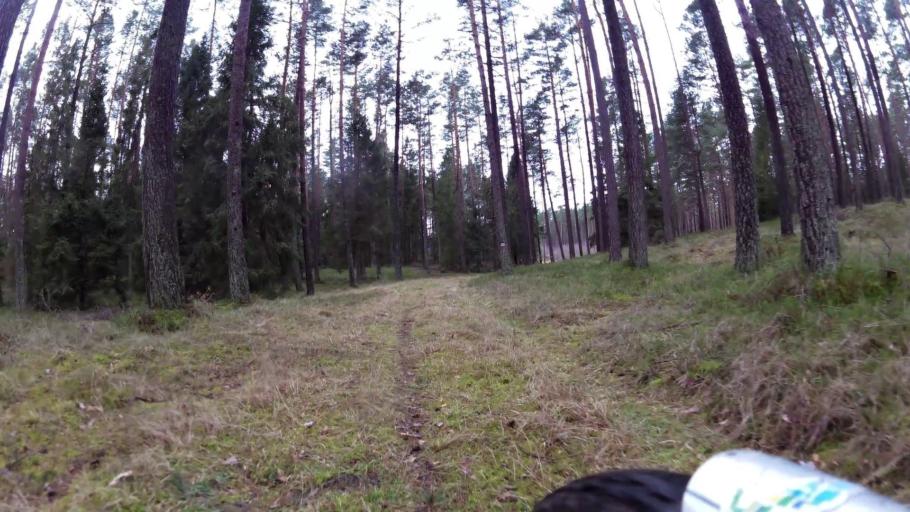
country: PL
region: Pomeranian Voivodeship
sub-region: Powiat bytowski
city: Kolczyglowy
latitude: 54.2423
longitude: 17.2749
